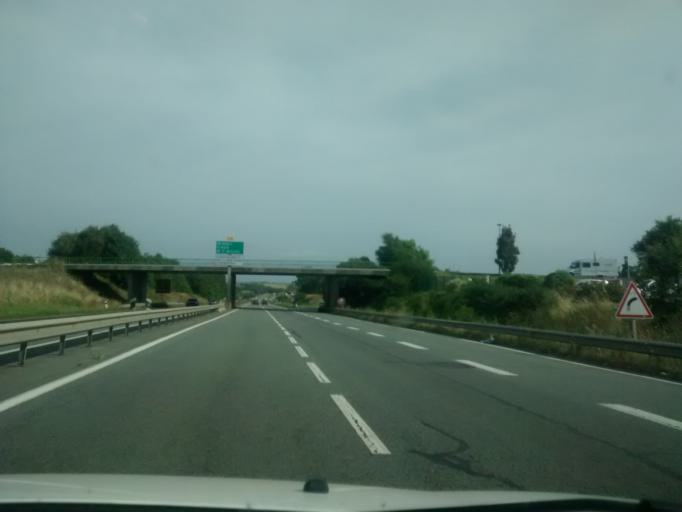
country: FR
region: Brittany
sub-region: Departement d'Ille-et-Vilaine
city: Saint-Jouan-des-Guerets
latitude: 48.6059
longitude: -1.9758
